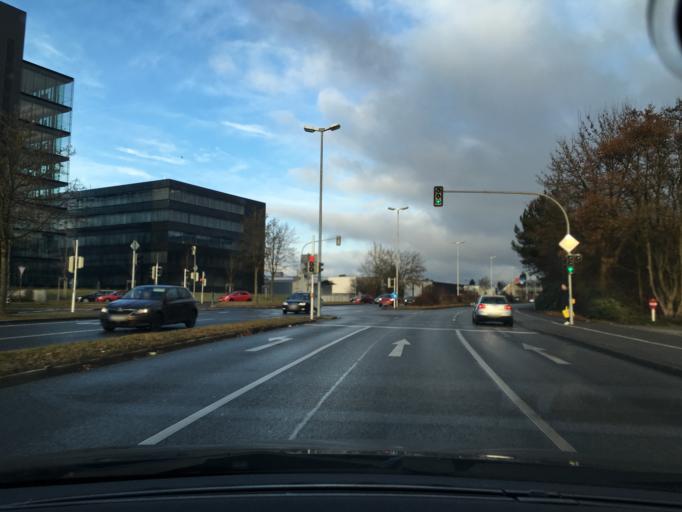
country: DE
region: Baden-Wuerttemberg
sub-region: Tuebingen Region
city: Weingarten
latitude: 47.7955
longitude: 9.6255
